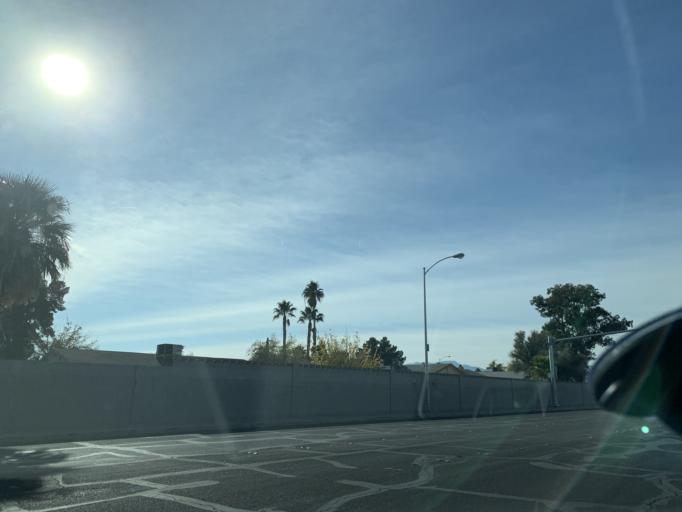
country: US
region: Nevada
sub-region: Clark County
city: Spring Valley
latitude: 36.1072
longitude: -115.2295
